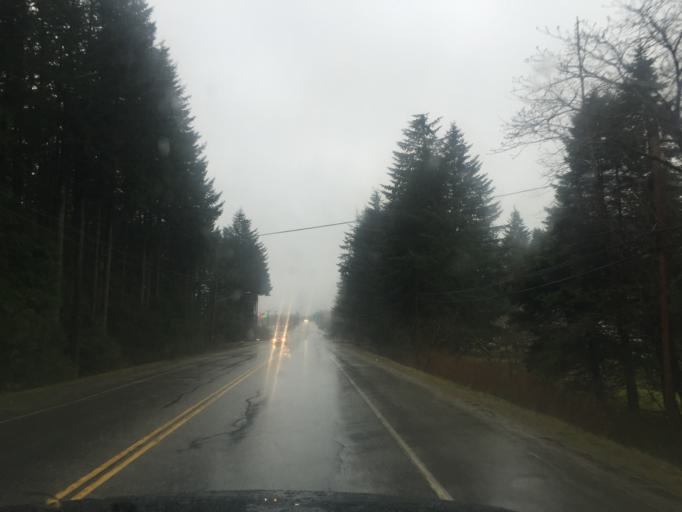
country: CA
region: British Columbia
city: Hope
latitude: 49.3629
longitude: -121.4726
